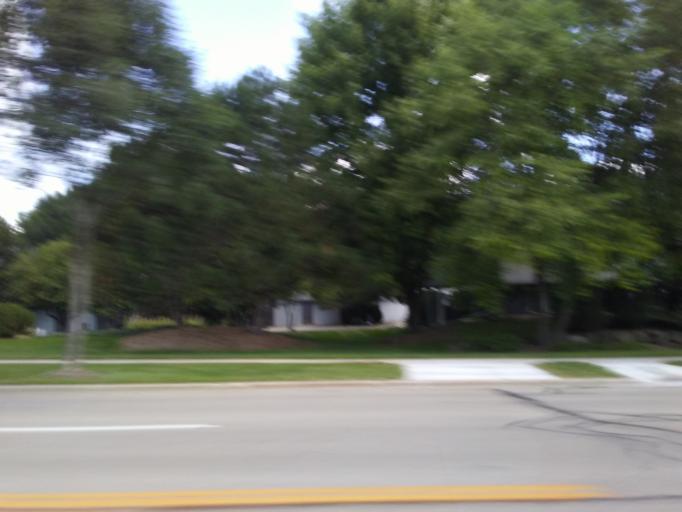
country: US
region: Wisconsin
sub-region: Dane County
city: Verona
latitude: 43.0316
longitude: -89.5022
